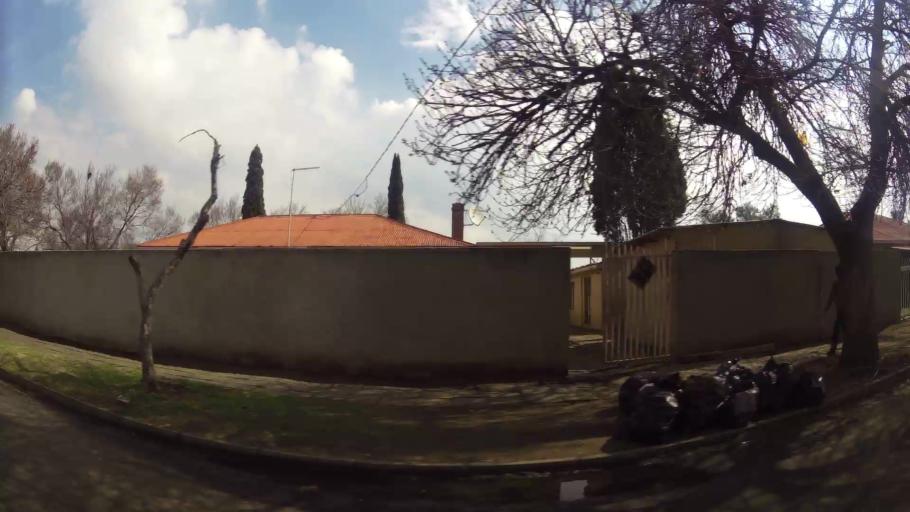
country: ZA
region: Gauteng
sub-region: Sedibeng District Municipality
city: Vereeniging
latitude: -26.6768
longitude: 27.9201
